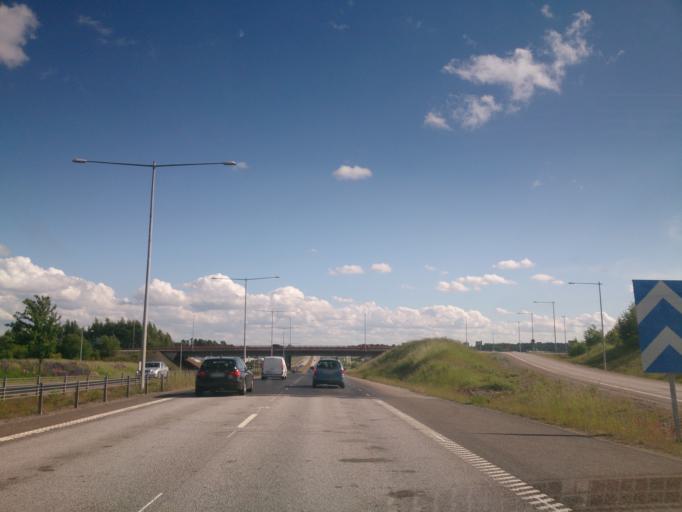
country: SE
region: OEstergoetland
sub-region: Norrkopings Kommun
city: Norrkoping
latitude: 58.6282
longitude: 16.1582
